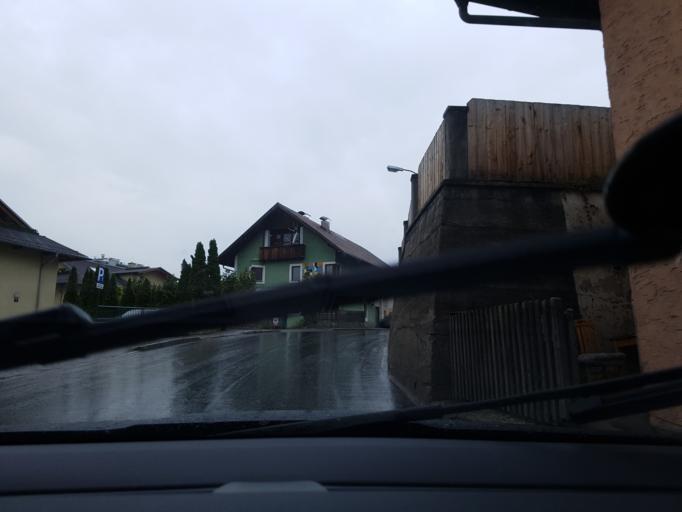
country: AT
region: Tyrol
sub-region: Politischer Bezirk Innsbruck Land
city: Telfs
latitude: 47.3103
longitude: 11.0644
